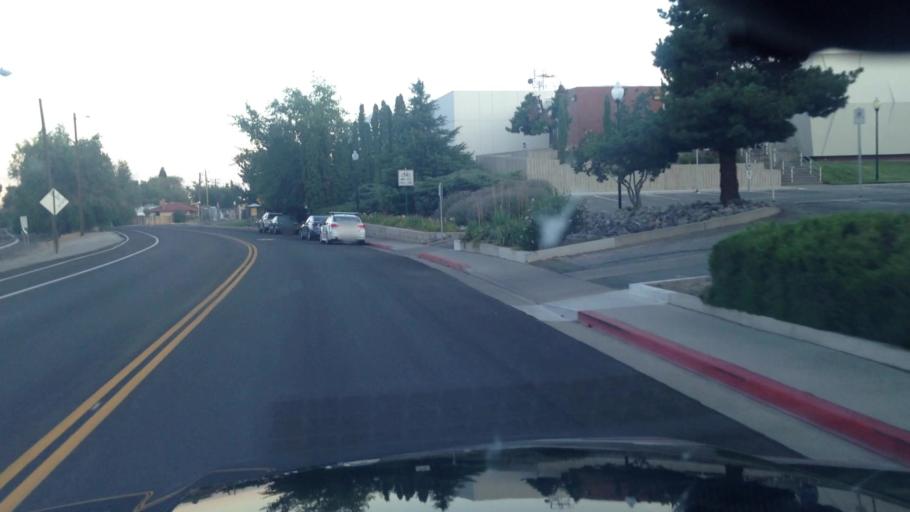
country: US
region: Nevada
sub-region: Washoe County
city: Reno
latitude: 39.5431
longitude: -119.8136
